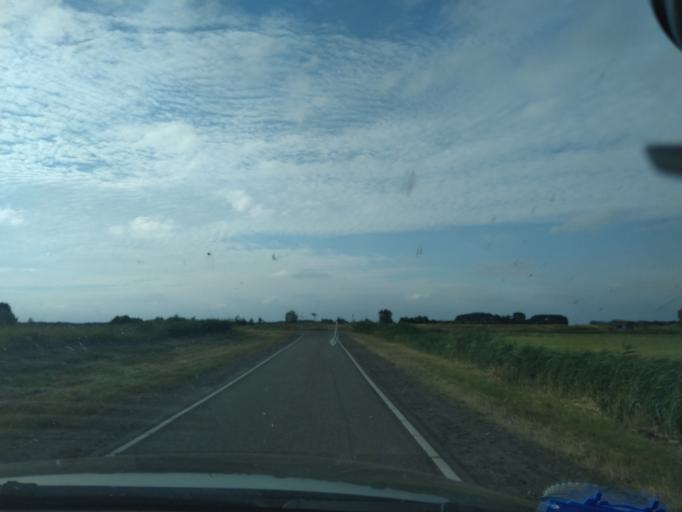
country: NL
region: Groningen
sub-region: Gemeente Vlagtwedde
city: Vlagtwedde
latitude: 53.0908
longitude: 7.1000
